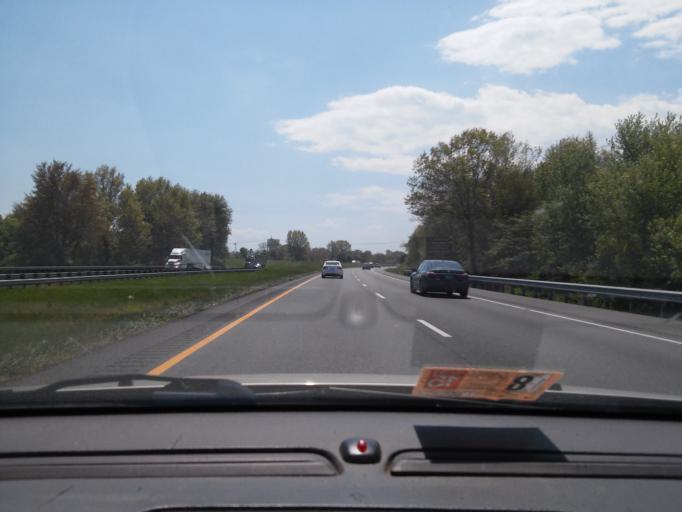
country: US
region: Maryland
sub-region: Washington County
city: Williamsport
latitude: 39.5947
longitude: -77.8091
